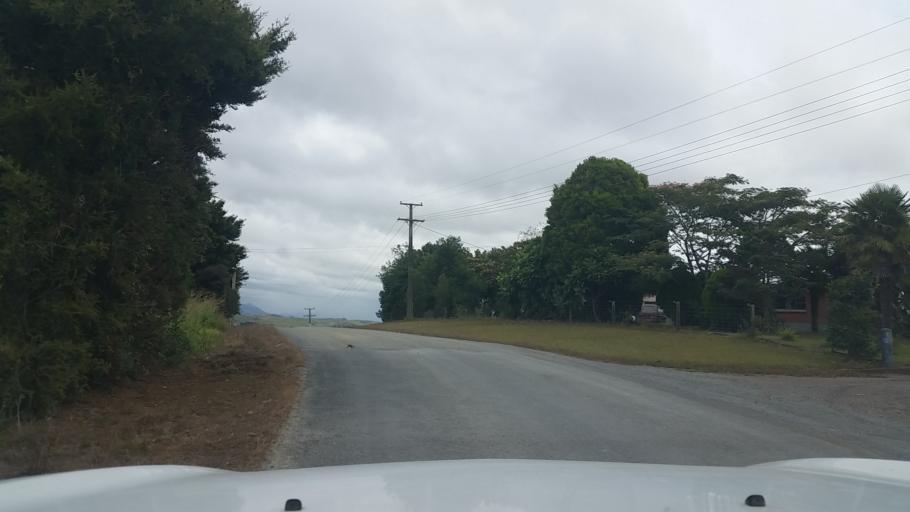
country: NZ
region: Northland
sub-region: Whangarei
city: Maungatapere
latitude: -35.6721
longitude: 174.1549
